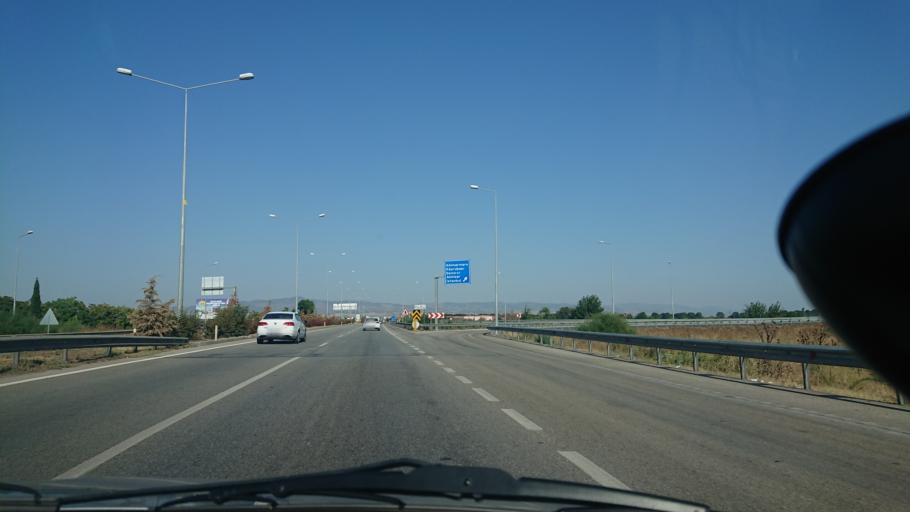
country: TR
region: Manisa
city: Salihli
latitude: 38.5001
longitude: 28.2040
